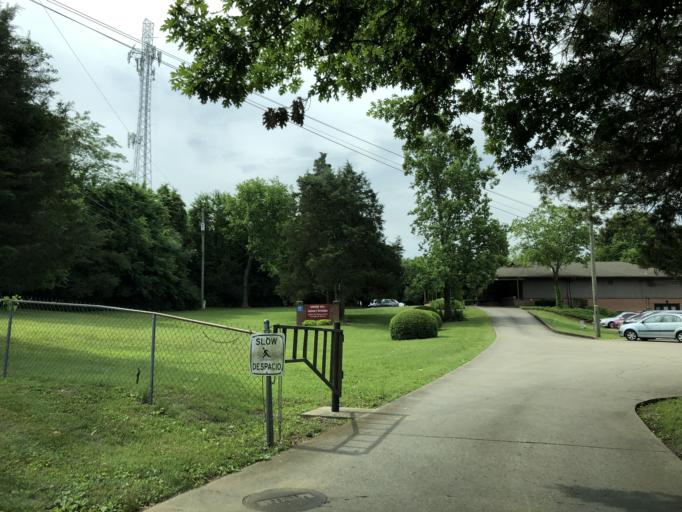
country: US
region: Tennessee
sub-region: Davidson County
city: Goodlettsville
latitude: 36.2804
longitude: -86.7152
